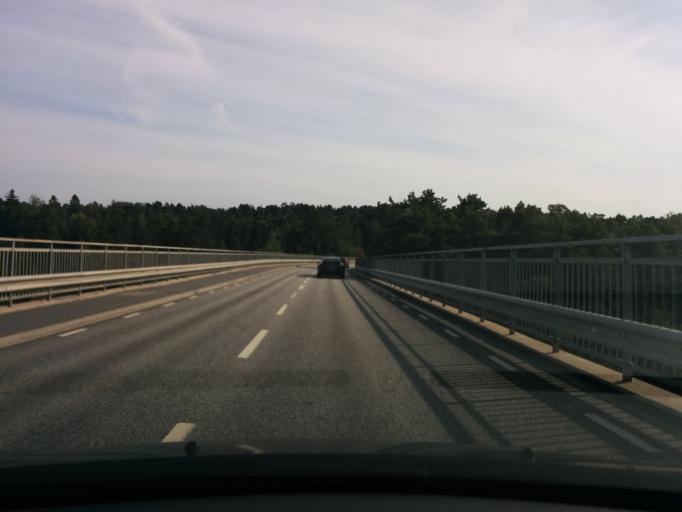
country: SE
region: Stockholm
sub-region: Varmdo Kommun
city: Holo
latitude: 59.2934
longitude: 18.6679
